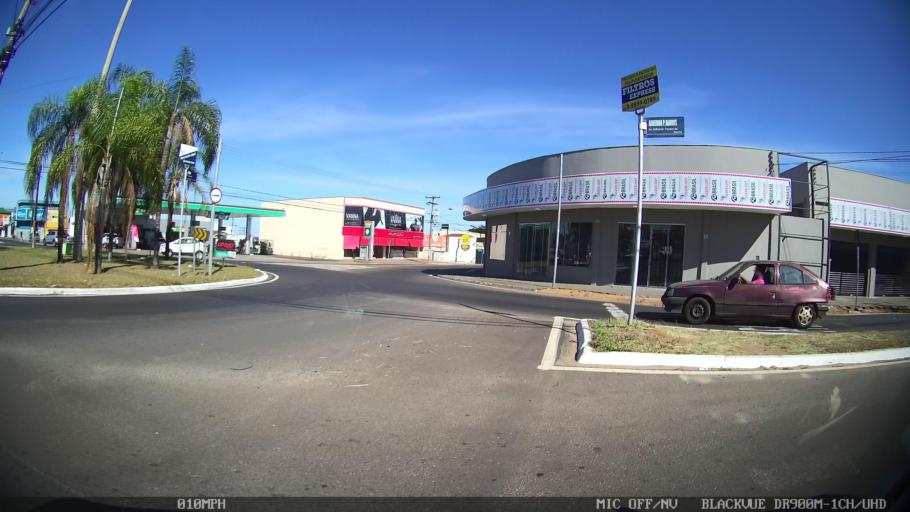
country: BR
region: Sao Paulo
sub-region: Franca
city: Franca
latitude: -20.5251
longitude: -47.3699
